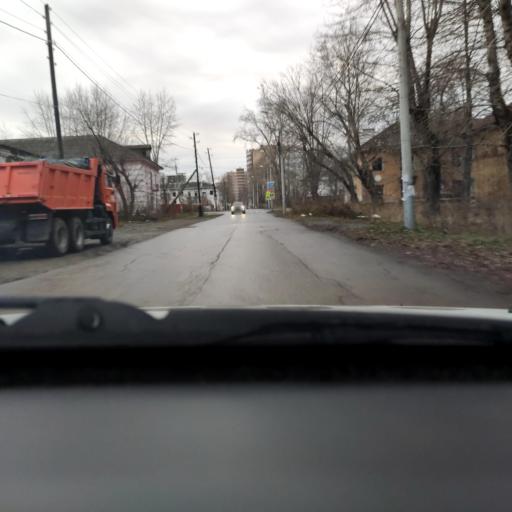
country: RU
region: Perm
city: Perm
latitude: 58.0006
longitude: 56.1842
